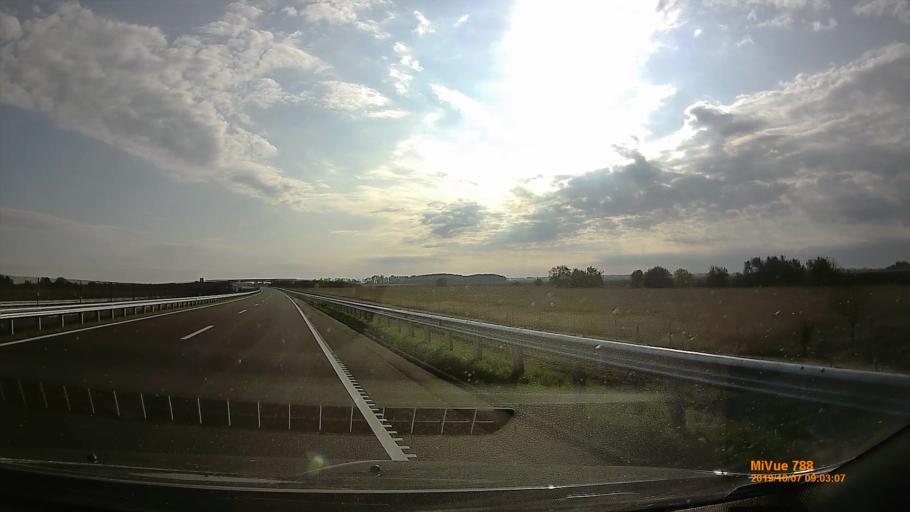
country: HU
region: Bekes
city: Szarvas
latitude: 46.8172
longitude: 20.5303
